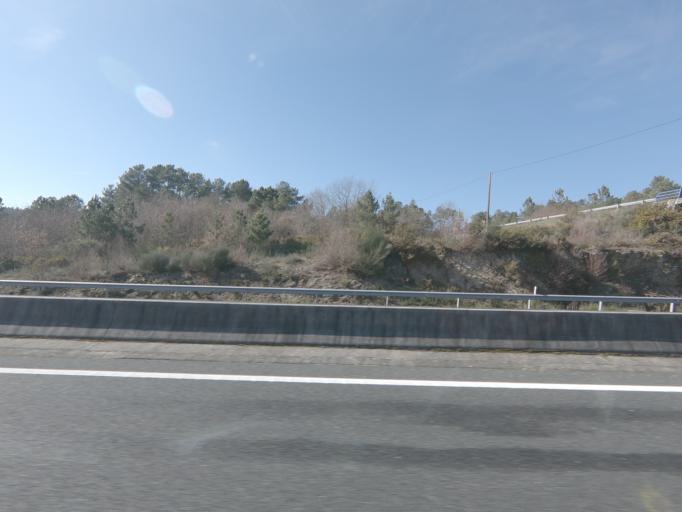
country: ES
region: Galicia
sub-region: Provincia de Ourense
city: Pinor
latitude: 42.5162
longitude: -8.0197
